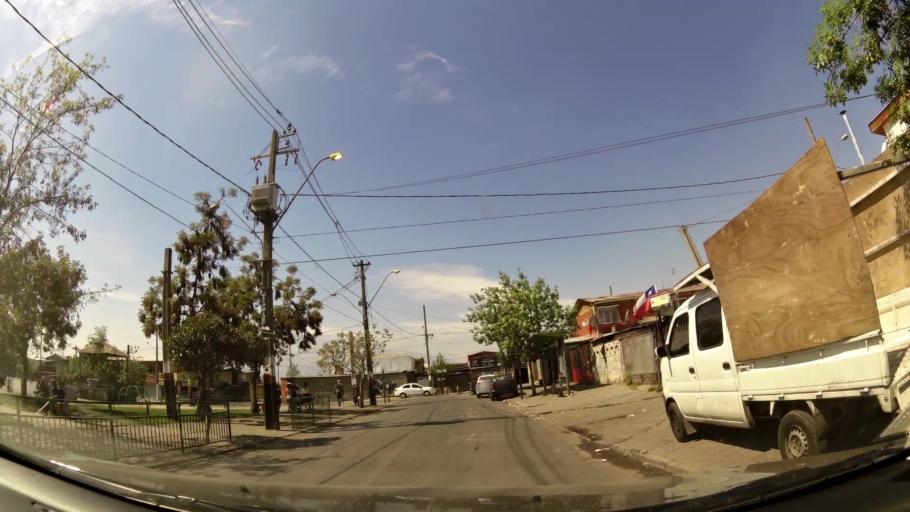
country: CL
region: Santiago Metropolitan
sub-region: Provincia de Santiago
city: La Pintana
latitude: -33.5909
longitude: -70.6160
